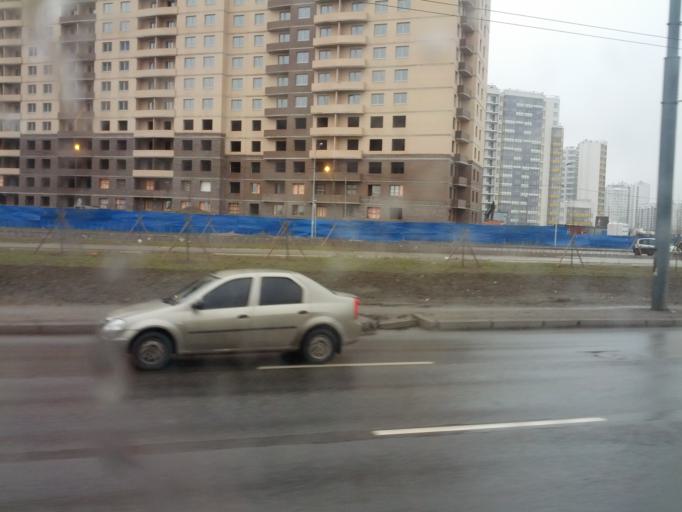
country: RU
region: St.-Petersburg
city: Krasnogvargeisky
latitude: 59.9146
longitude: 30.4339
